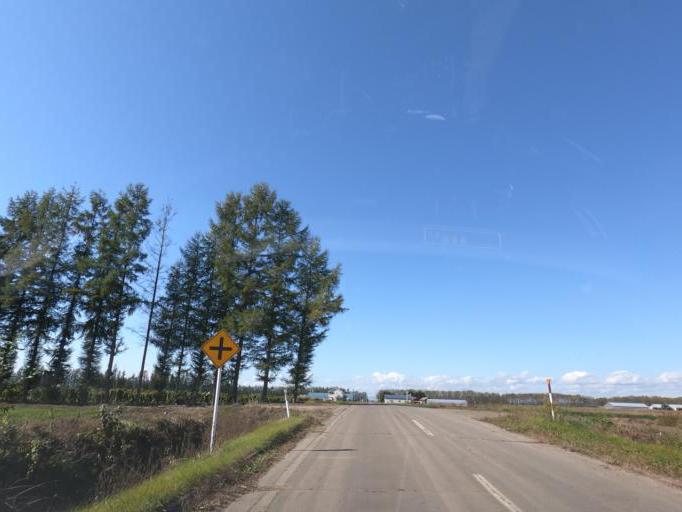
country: JP
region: Hokkaido
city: Otofuke
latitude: 43.0601
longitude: 143.2706
